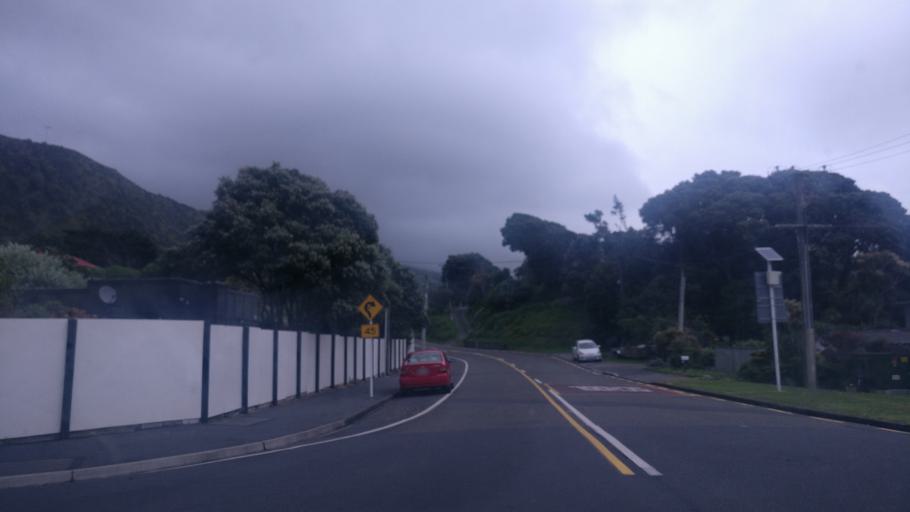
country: NZ
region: Wellington
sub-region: Kapiti Coast District
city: Paraparaumu
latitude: -40.9827
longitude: 174.9562
